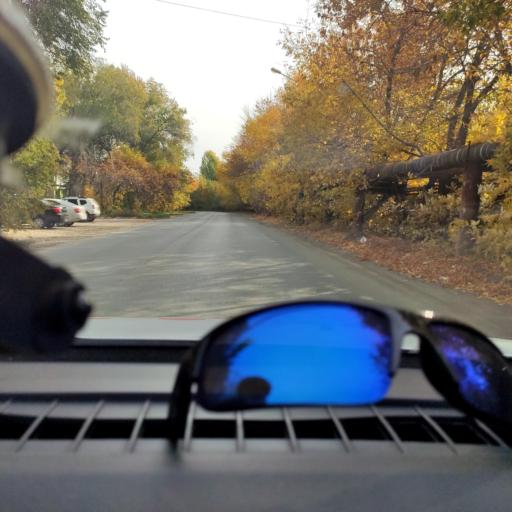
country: RU
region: Samara
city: Samara
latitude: 53.1192
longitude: 50.0903
